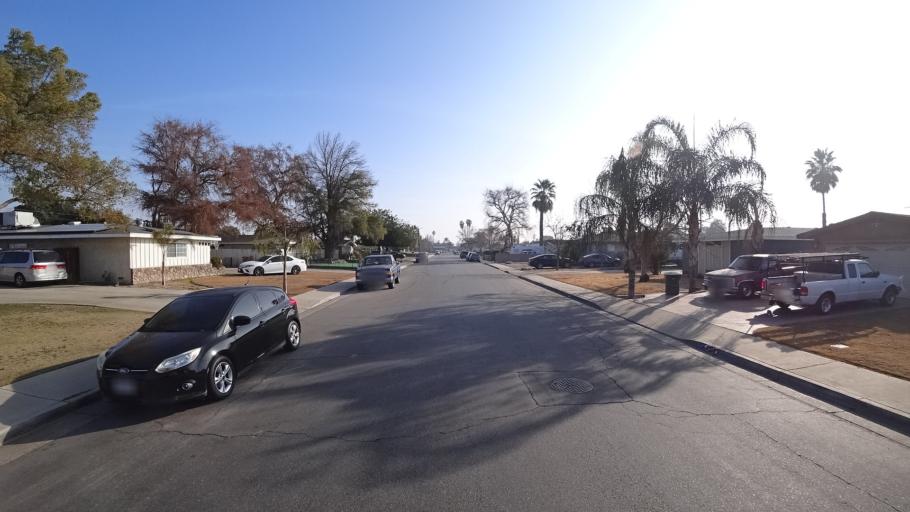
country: US
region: California
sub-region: Kern County
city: Bakersfield
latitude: 35.3289
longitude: -119.0289
